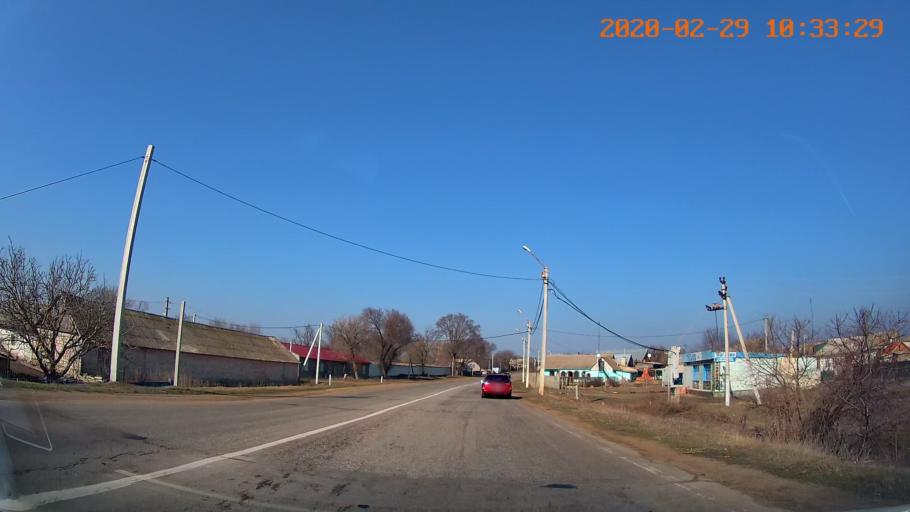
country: MD
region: Anenii Noi
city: Varnita
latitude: 46.9706
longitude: 29.5439
